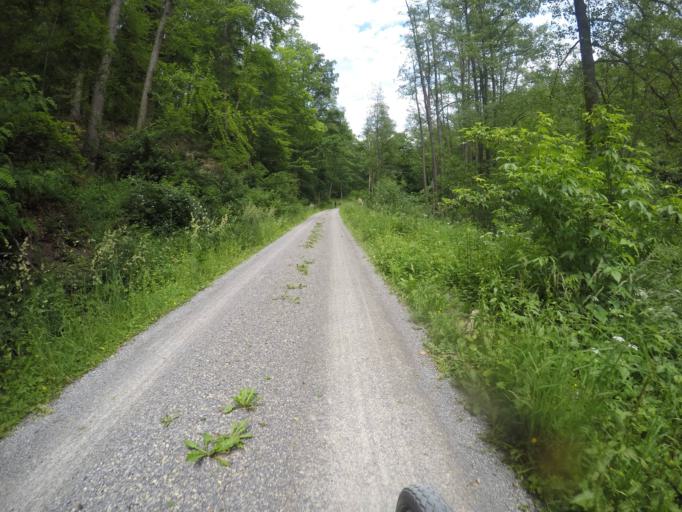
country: DE
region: Baden-Wuerttemberg
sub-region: Regierungsbezirk Stuttgart
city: Hildrizhausen
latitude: 48.5990
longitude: 8.9779
